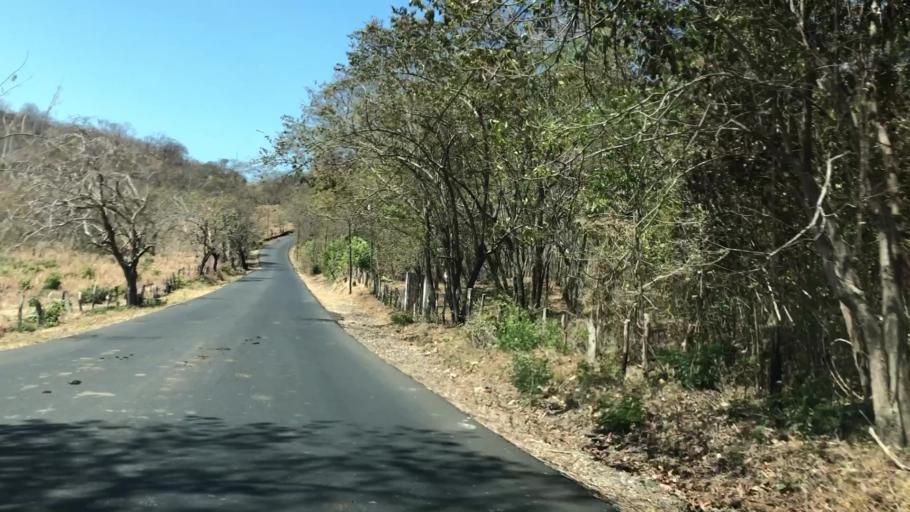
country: CR
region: Guanacaste
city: Belen
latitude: 10.3509
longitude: -85.8185
